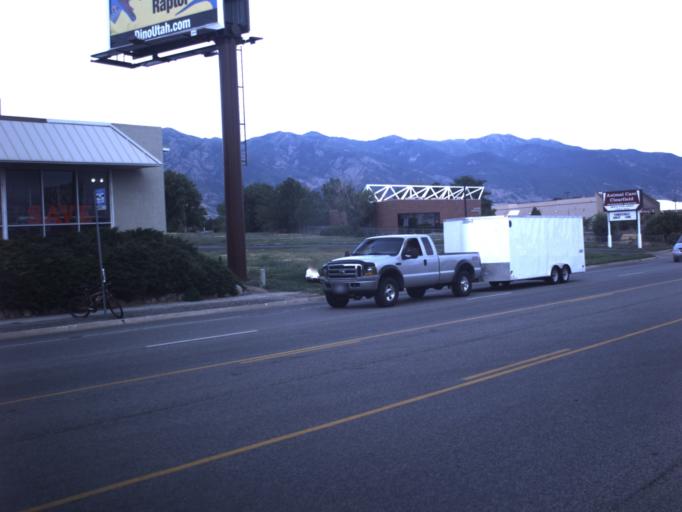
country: US
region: Utah
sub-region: Davis County
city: Clearfield
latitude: 41.0922
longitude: -112.0043
